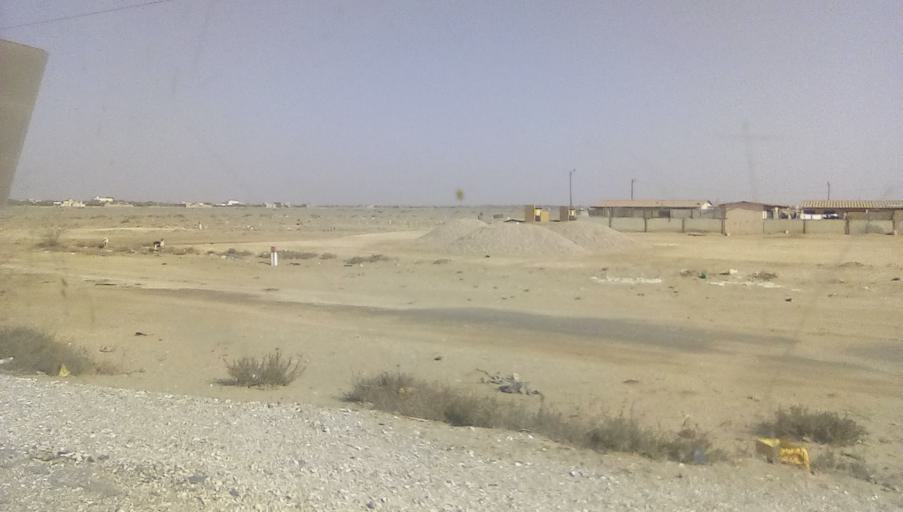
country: SN
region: Saint-Louis
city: Saint-Louis
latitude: 16.0386
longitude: -16.4559
